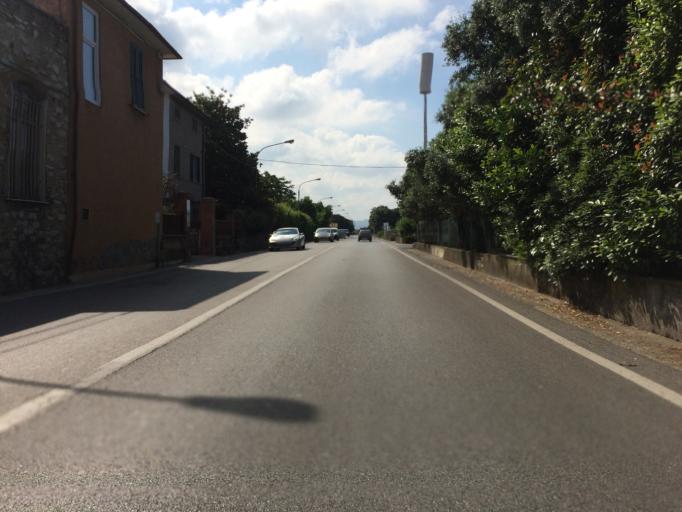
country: IT
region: Tuscany
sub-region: Provincia di Lucca
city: Ripa-Pozzi-Querceta-Ponterosso
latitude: 43.9748
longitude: 10.2027
